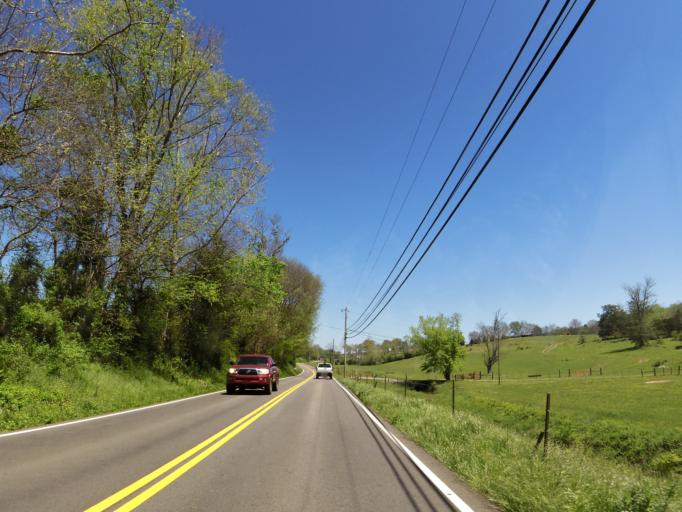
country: US
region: Tennessee
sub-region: Greene County
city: Mosheim
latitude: 36.0887
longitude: -82.9451
